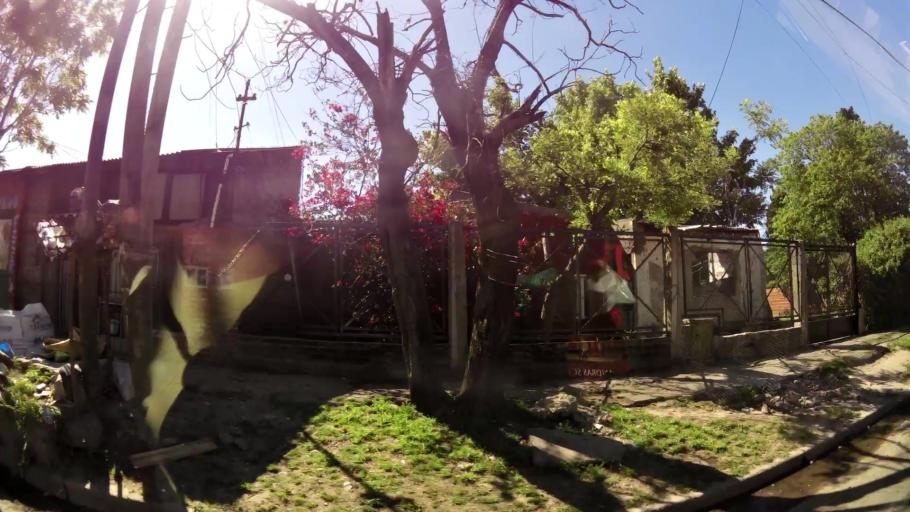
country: AR
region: Buenos Aires
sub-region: Partido de Almirante Brown
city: Adrogue
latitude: -34.7885
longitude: -58.3608
